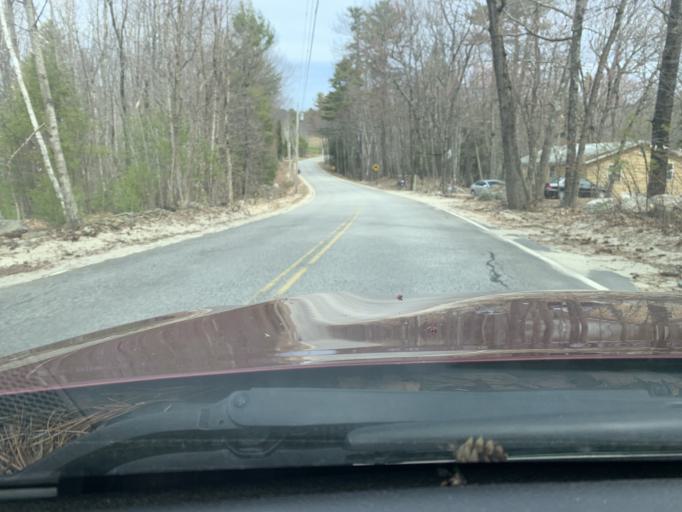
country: US
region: Maine
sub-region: Cumberland County
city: Raymond
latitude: 43.9489
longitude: -70.3863
